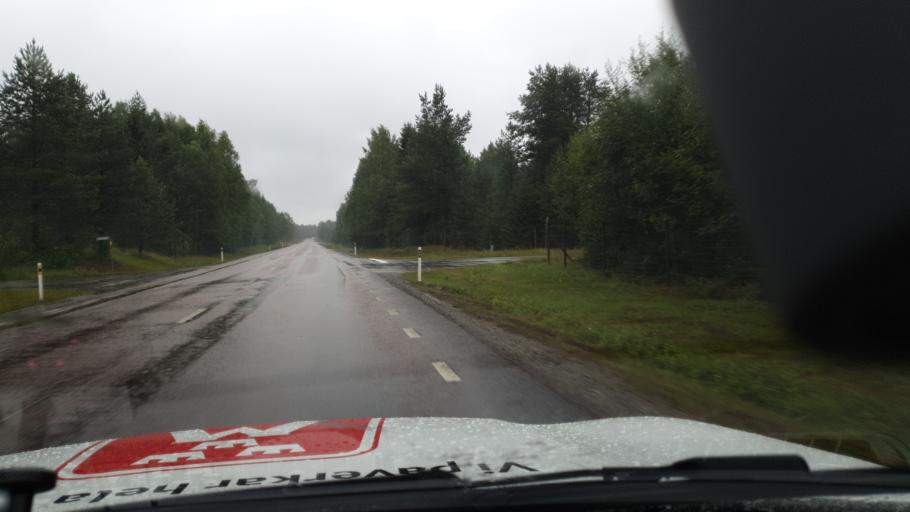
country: SE
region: Vaesterbotten
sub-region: Skelleftea Kommun
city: Burea
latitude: 64.6046
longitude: 21.1990
